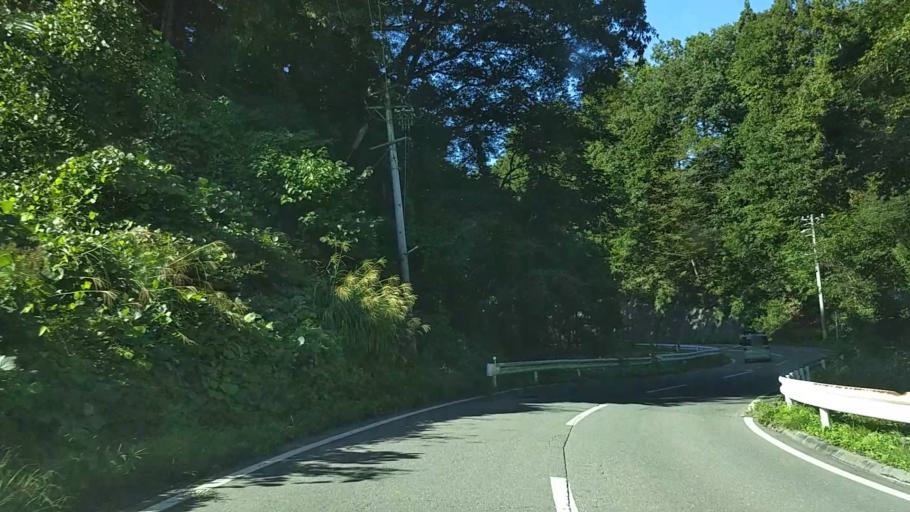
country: JP
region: Nagano
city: Nagano-shi
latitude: 36.6022
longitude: 138.0941
